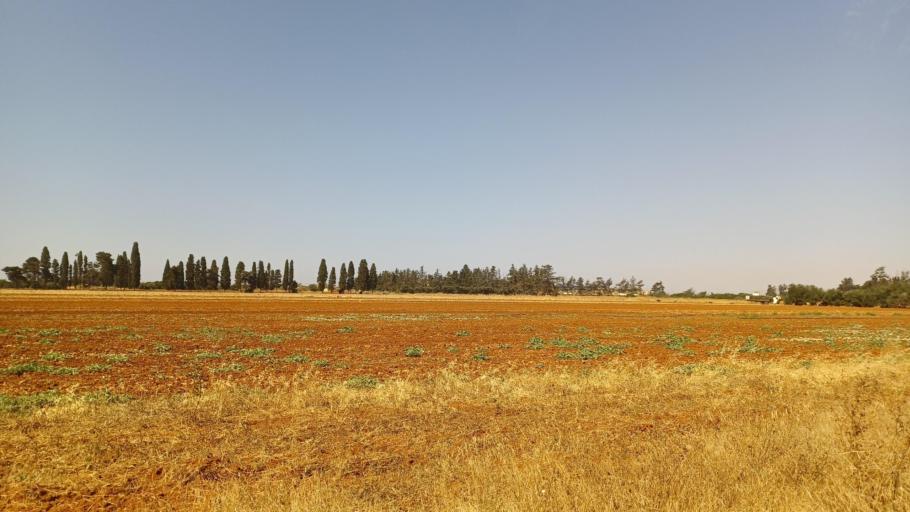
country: CY
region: Ammochostos
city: Avgorou
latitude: 35.0078
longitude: 33.8147
